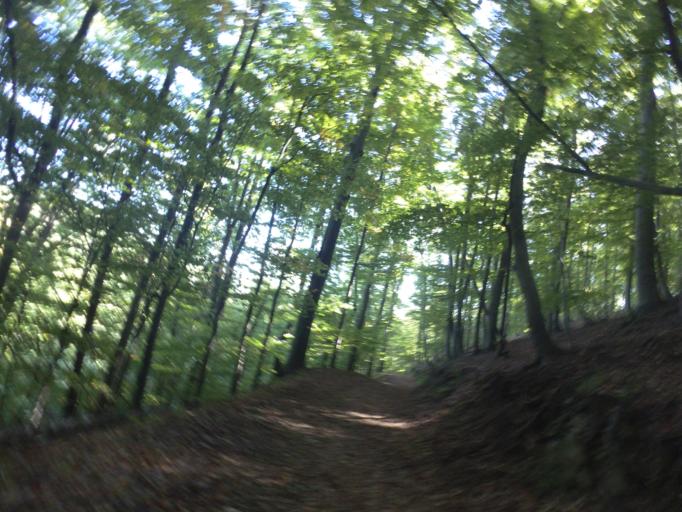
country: AT
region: Styria
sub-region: Politischer Bezirk Leibnitz
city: Kitzeck im Sausal
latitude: 46.7870
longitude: 15.4342
